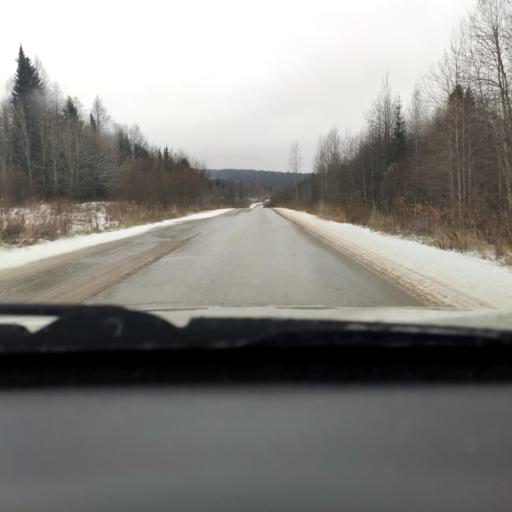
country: RU
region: Perm
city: Ferma
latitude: 57.9817
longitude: 56.3607
